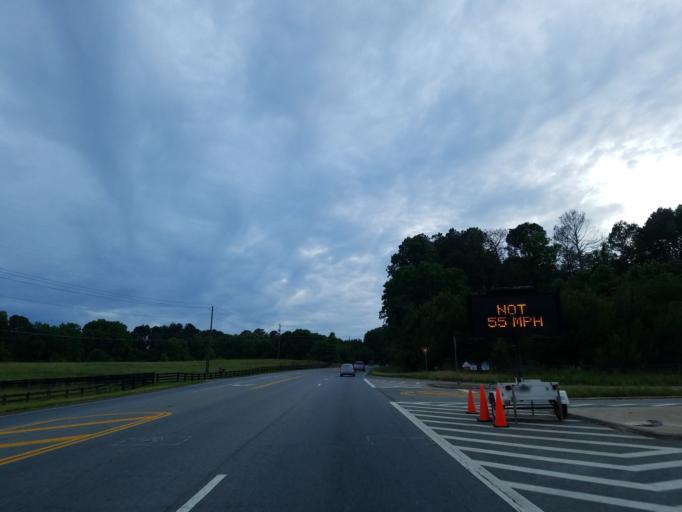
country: US
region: Georgia
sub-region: Cherokee County
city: Ball Ground
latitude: 34.2566
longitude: -84.3211
